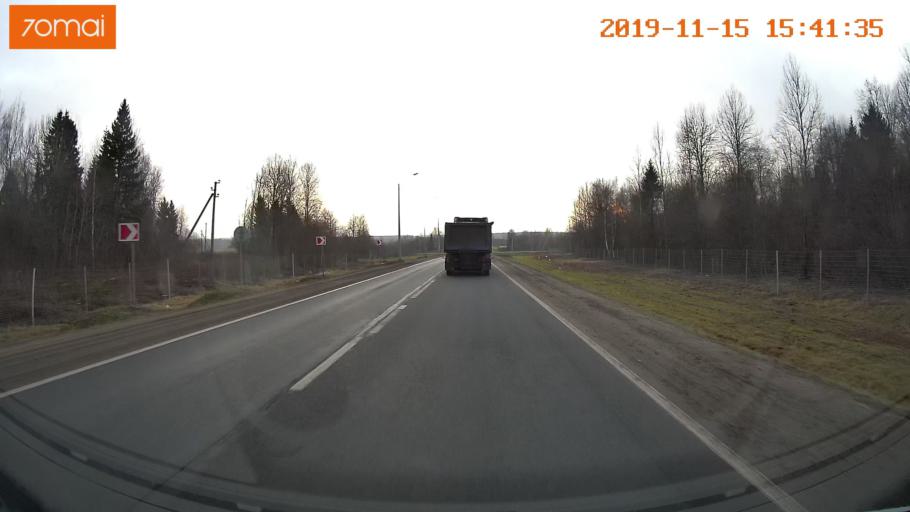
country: RU
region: Jaroslavl
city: Danilov
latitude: 57.9994
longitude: 40.0470
